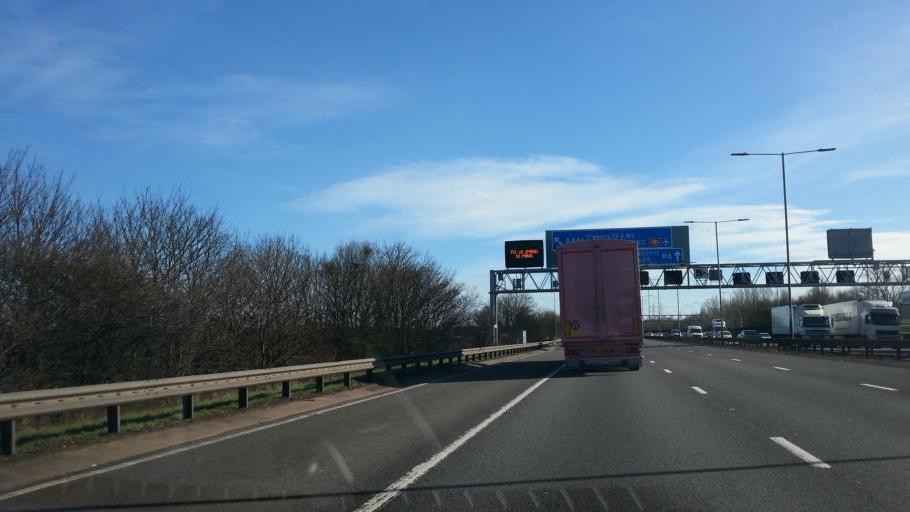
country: GB
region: England
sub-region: Solihull
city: Chelmsley Wood
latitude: 52.4858
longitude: -1.7261
